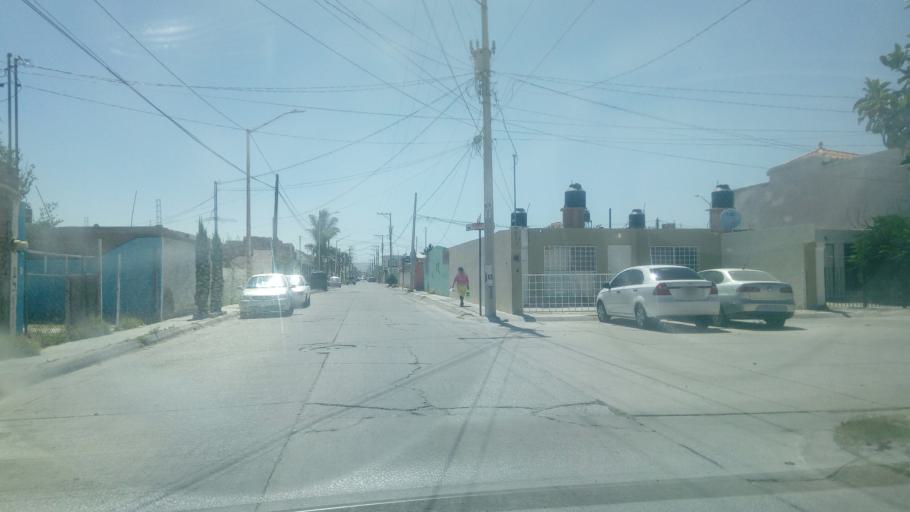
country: MX
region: Durango
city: Victoria de Durango
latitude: 24.0036
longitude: -104.6252
